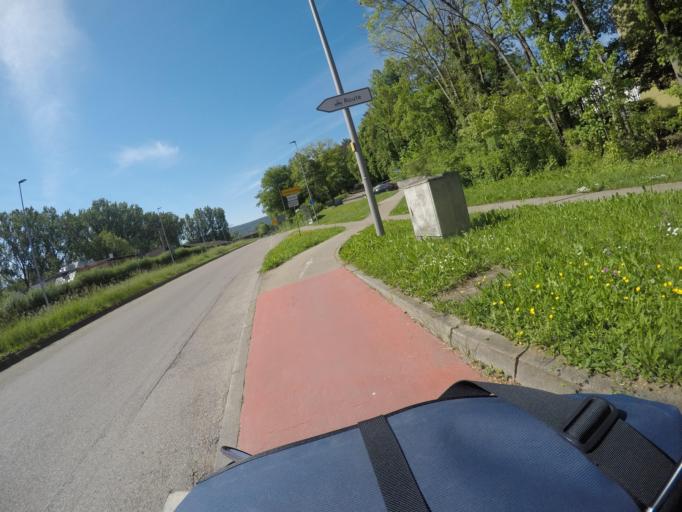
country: DE
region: Baden-Wuerttemberg
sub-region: Regierungsbezirk Stuttgart
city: Aalen
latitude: 48.8589
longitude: 10.0986
